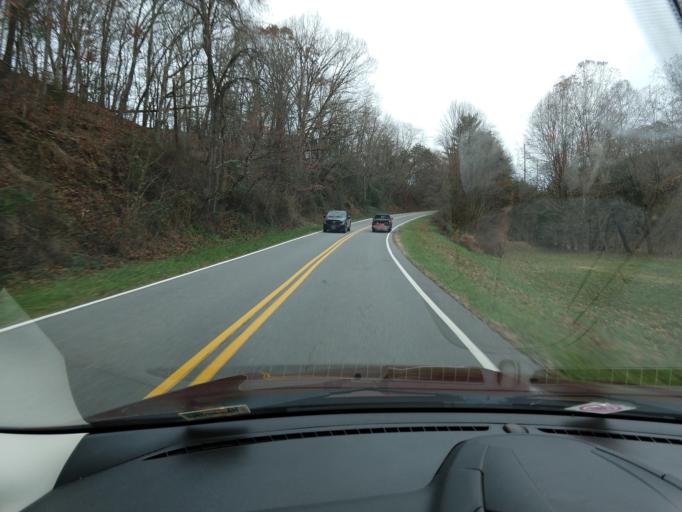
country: US
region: Virginia
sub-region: City of Covington
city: Covington
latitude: 37.7814
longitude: -80.1059
